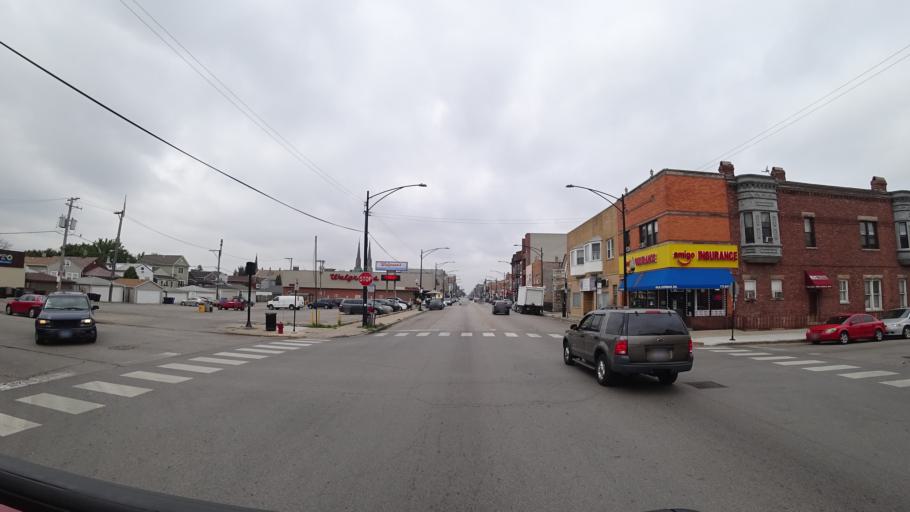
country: US
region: Illinois
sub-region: Cook County
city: Chicago
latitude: 41.8522
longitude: -87.6733
